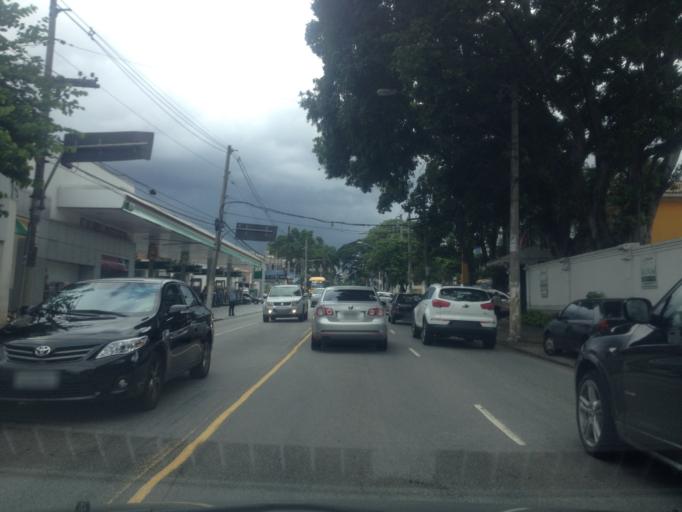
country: BR
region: Sao Paulo
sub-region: Sao Paulo
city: Sao Paulo
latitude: -23.5798
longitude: -46.6828
